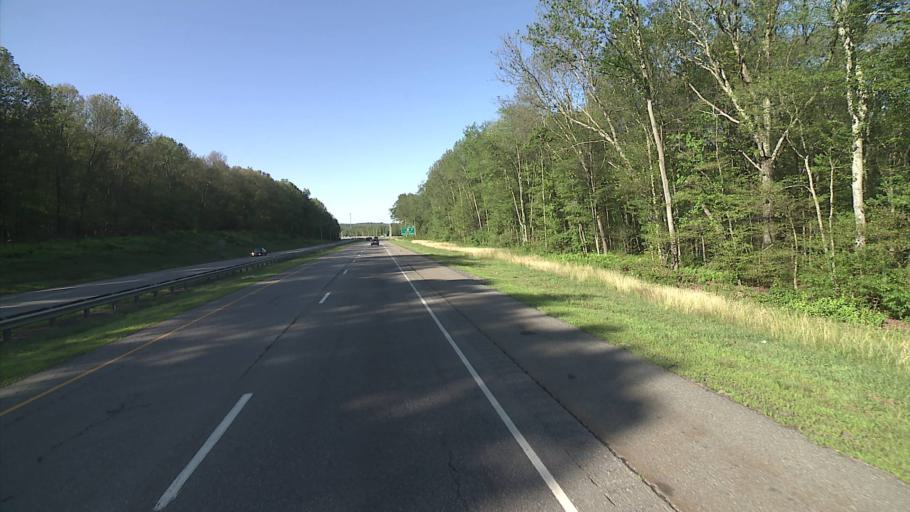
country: US
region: Connecticut
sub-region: Windham County
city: Moosup
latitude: 41.7249
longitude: -71.8917
